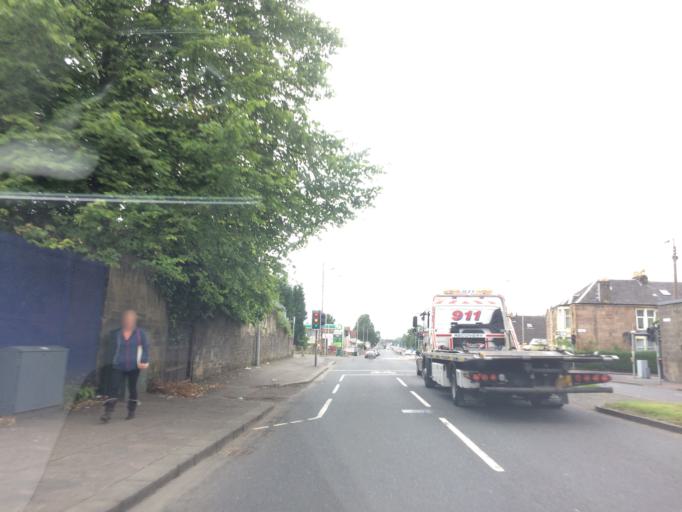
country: GB
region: Scotland
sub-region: East Renfrewshire
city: Giffnock
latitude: 55.8542
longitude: -4.3225
